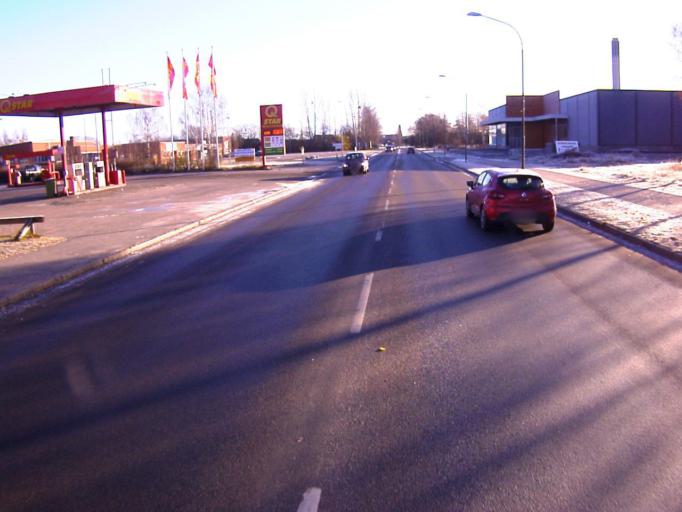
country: SE
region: Soedermanland
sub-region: Eskilstuna Kommun
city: Eskilstuna
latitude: 59.3842
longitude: 16.4926
